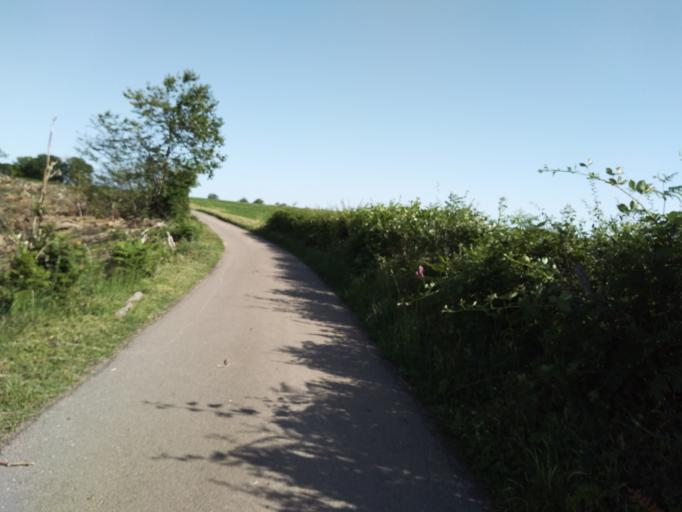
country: FR
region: Bourgogne
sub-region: Departement de la Cote-d'Or
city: Saulieu
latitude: 47.2807
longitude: 4.1509
